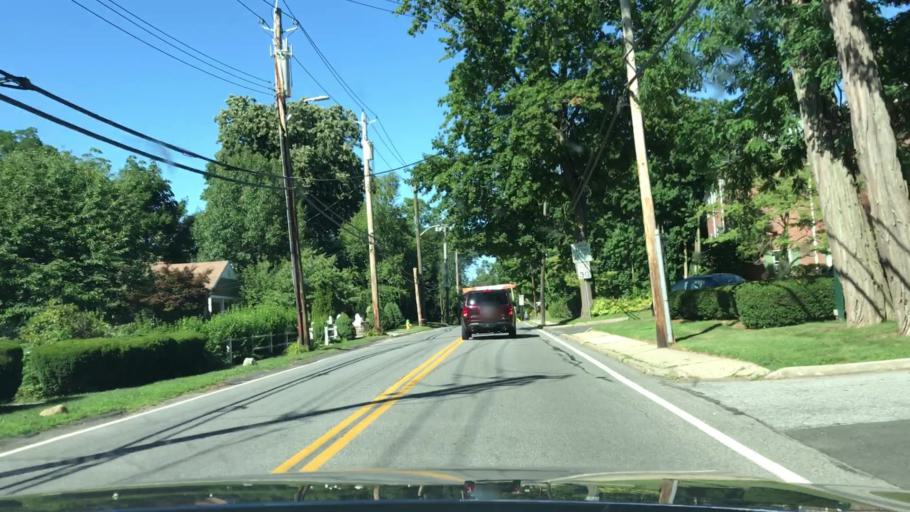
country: US
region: New York
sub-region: Westchester County
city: Pleasantville
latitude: 41.1300
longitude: -73.7976
